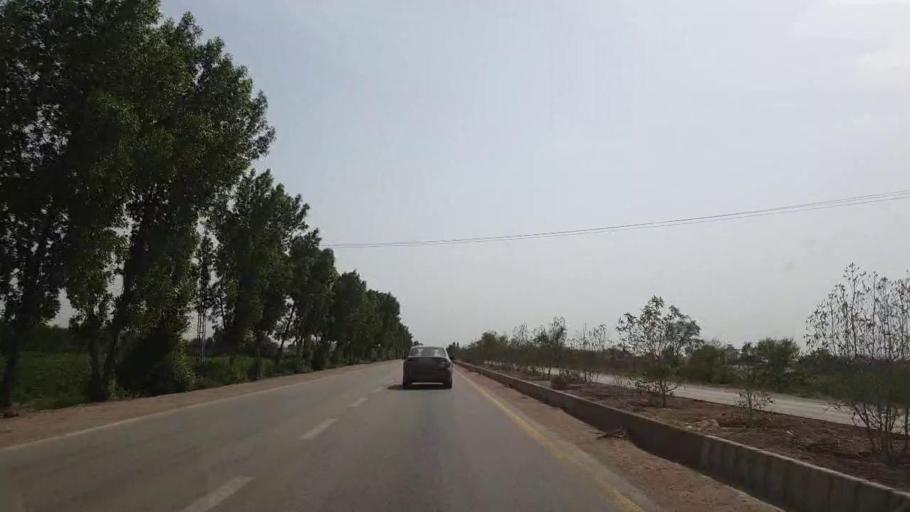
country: PK
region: Sindh
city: Sakrand
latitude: 26.2088
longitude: 68.3227
